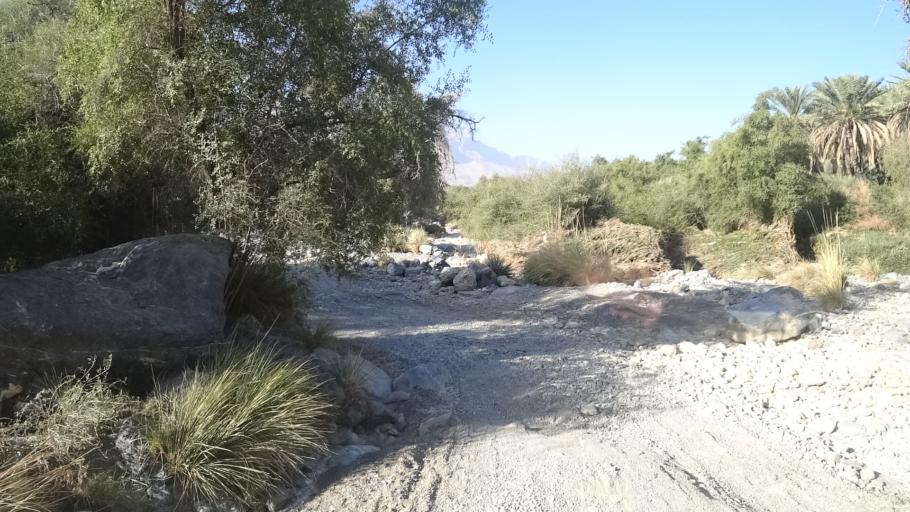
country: OM
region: Muhafazat ad Dakhiliyah
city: Bahla'
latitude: 23.2304
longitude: 57.0691
